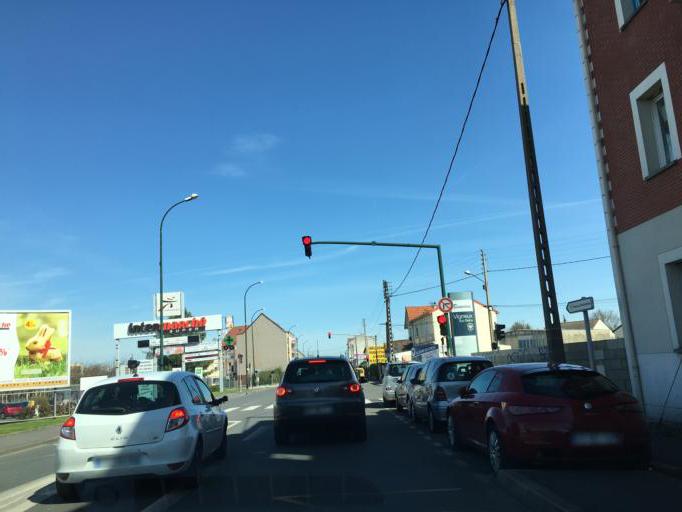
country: FR
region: Ile-de-France
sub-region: Departement de l'Essonne
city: Vigneux-sur-Seine
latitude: 48.6966
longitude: 2.4153
